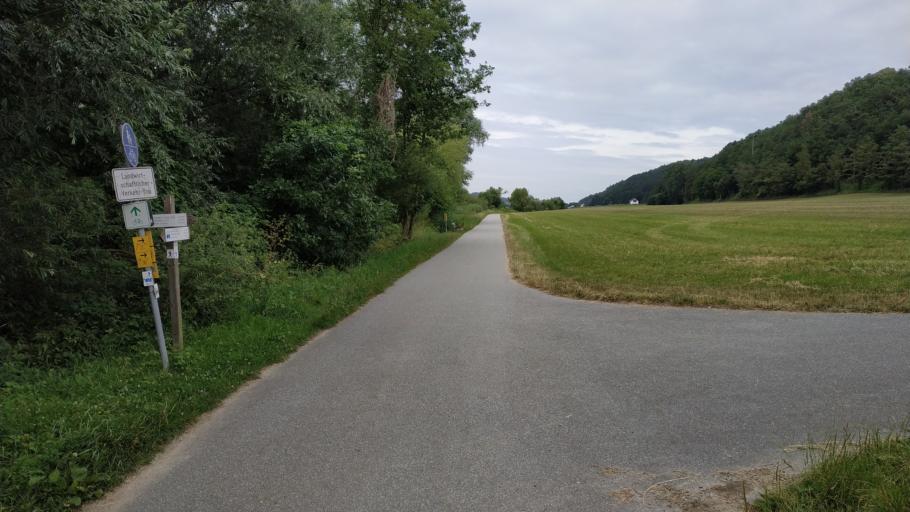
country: DE
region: Bavaria
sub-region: Lower Bavaria
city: Vilshofen
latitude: 48.6287
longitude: 13.2100
